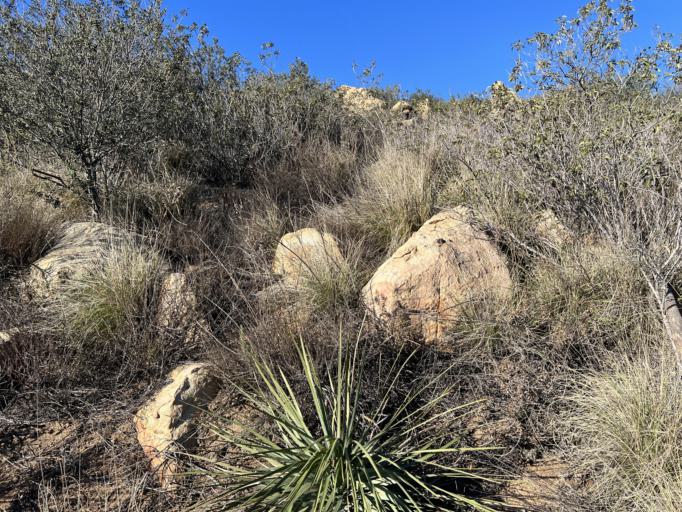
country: US
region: California
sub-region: San Diego County
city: Poway
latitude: 33.0275
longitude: -116.9985
